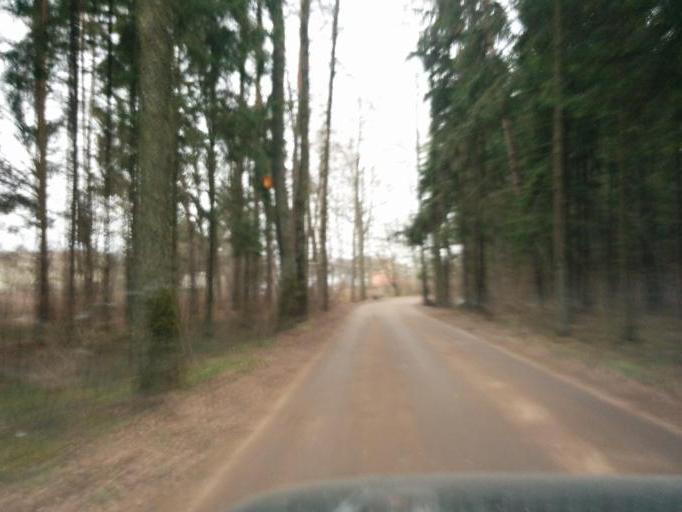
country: LV
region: Babite
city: Pinki
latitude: 56.9716
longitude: 23.8459
